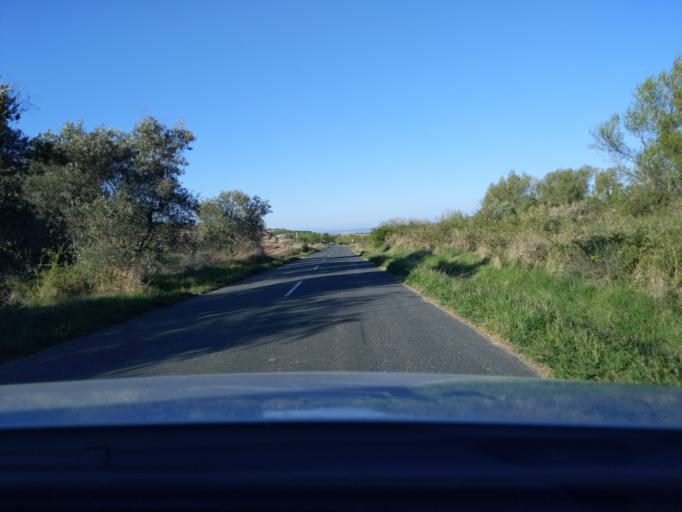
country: ES
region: La Rioja
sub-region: Provincia de La Rioja
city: Bergasa
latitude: 42.2610
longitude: -2.1102
